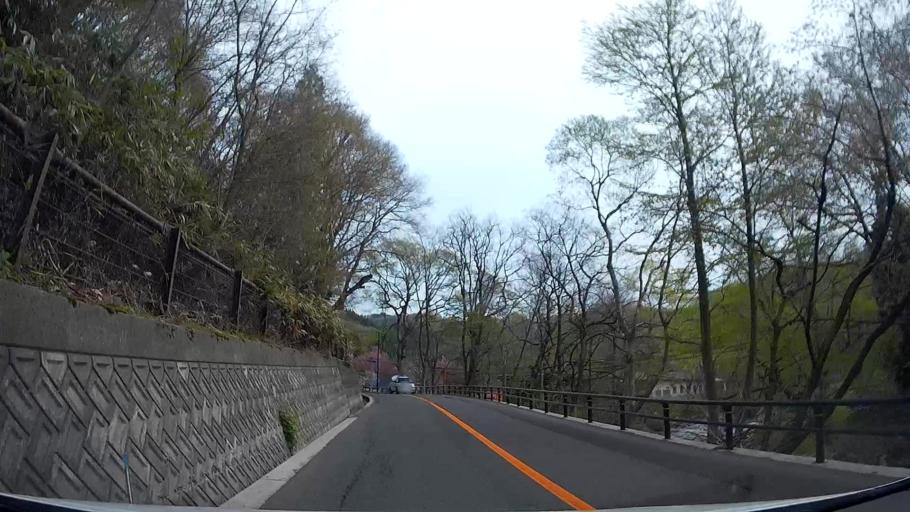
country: JP
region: Akita
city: Hanawa
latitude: 40.3744
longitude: 140.8834
